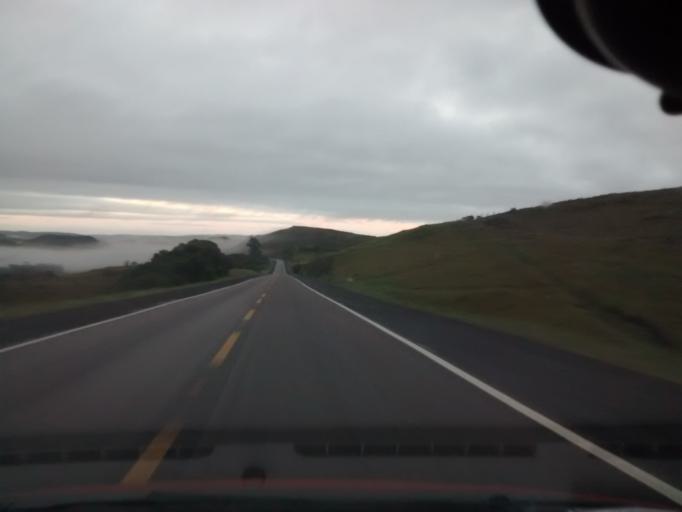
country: BR
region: Rio Grande do Sul
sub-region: Vacaria
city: Estrela
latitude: -28.1736
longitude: -50.6903
